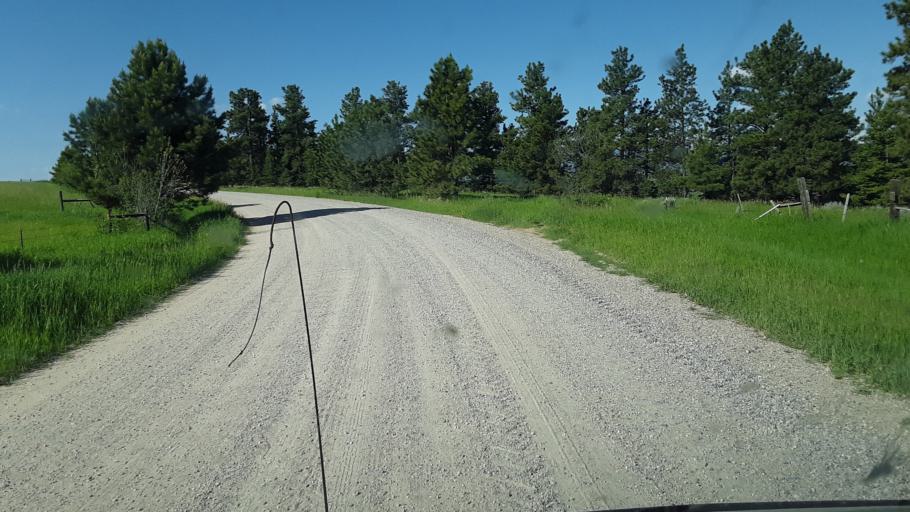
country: US
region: Montana
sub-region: Carbon County
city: Red Lodge
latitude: 45.3579
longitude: -109.1585
